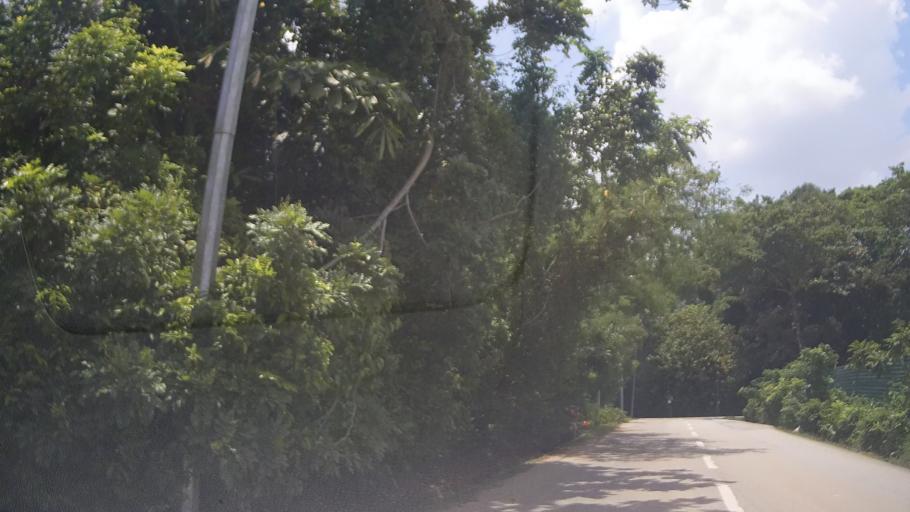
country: MY
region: Johor
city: Kampung Pasir Gudang Baru
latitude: 1.3943
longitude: 103.8677
